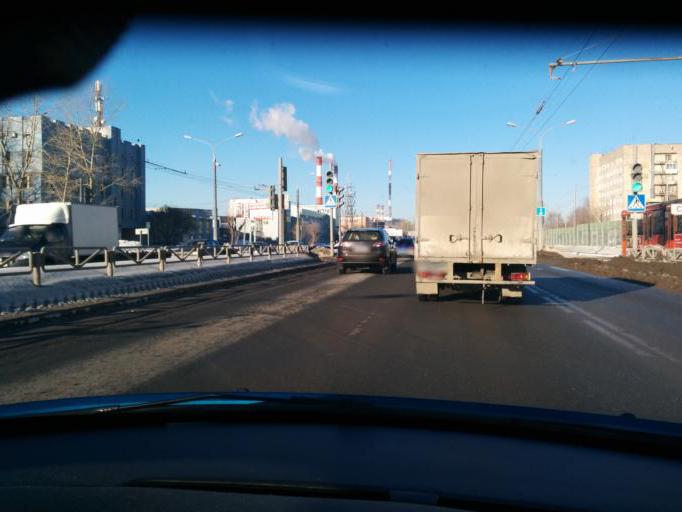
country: RU
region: Perm
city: Perm
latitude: 57.9700
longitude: 56.2614
